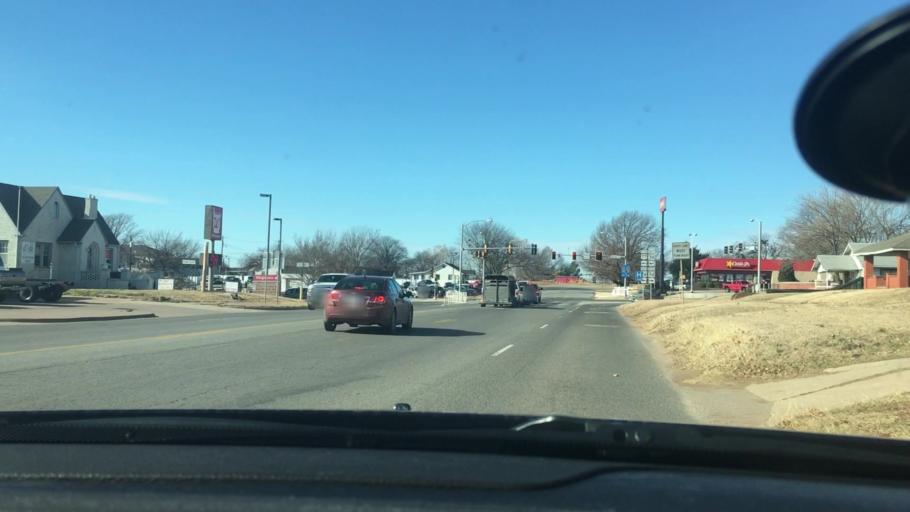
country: US
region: Oklahoma
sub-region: McClain County
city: Purcell
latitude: 35.0138
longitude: -97.3646
